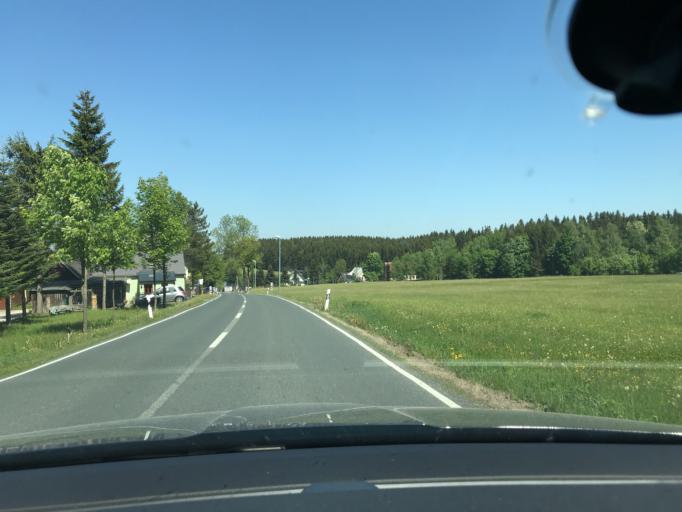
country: CZ
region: Ustecky
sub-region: Okres Chomutov
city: Vejprty
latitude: 50.4654
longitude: 12.9908
